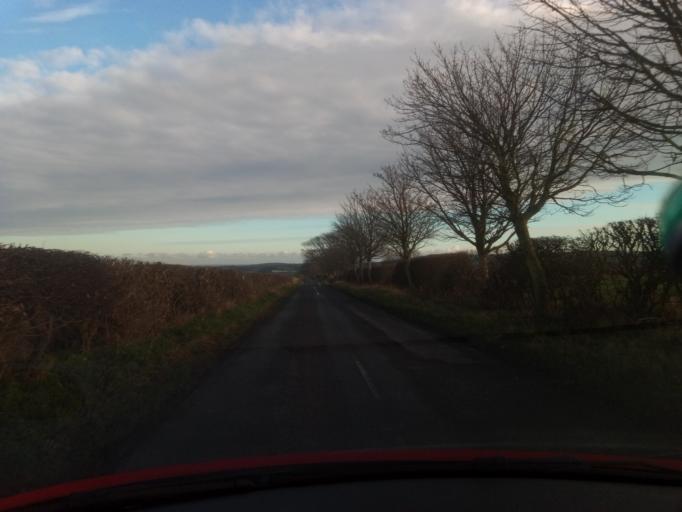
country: GB
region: Scotland
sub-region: The Scottish Borders
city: Chirnside
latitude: 55.8393
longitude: -2.1968
